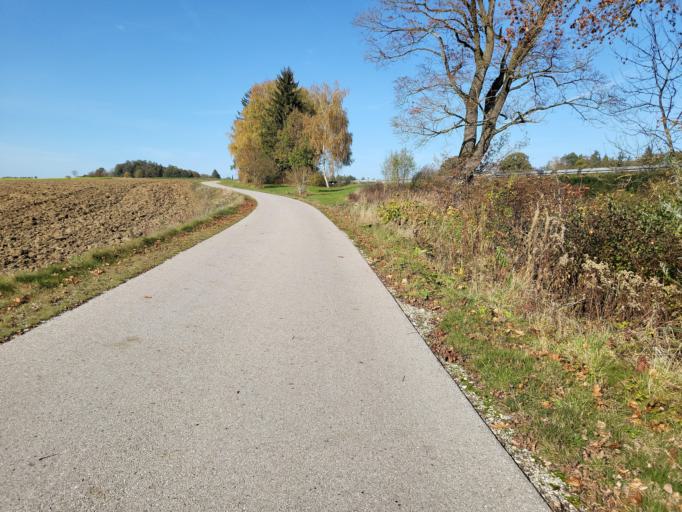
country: DE
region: Bavaria
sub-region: Upper Bavaria
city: Alling
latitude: 48.1607
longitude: 11.2852
